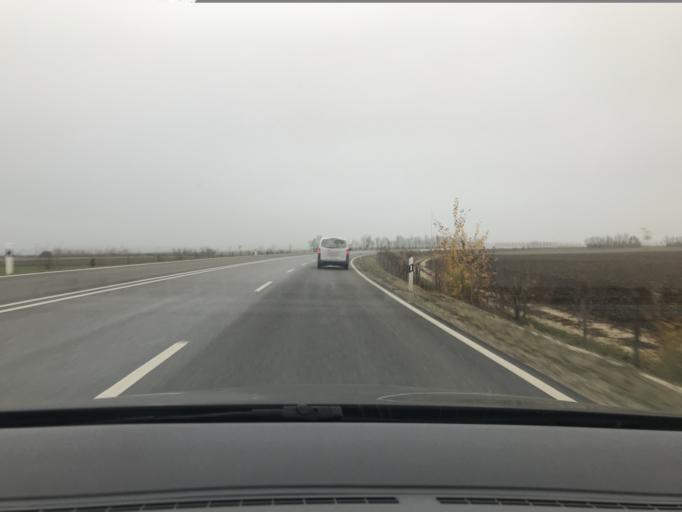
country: DE
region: Bavaria
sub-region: Swabia
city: Wallerstein
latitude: 48.8717
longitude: 10.4596
